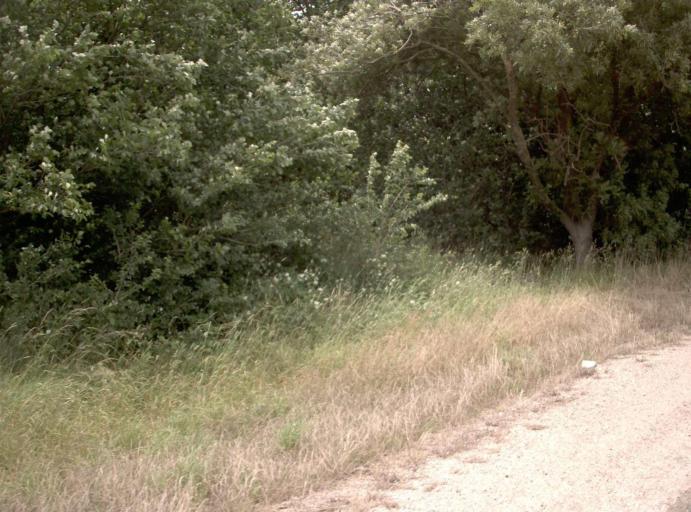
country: AU
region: Victoria
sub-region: Wellington
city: Sale
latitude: -37.9919
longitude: 146.9976
